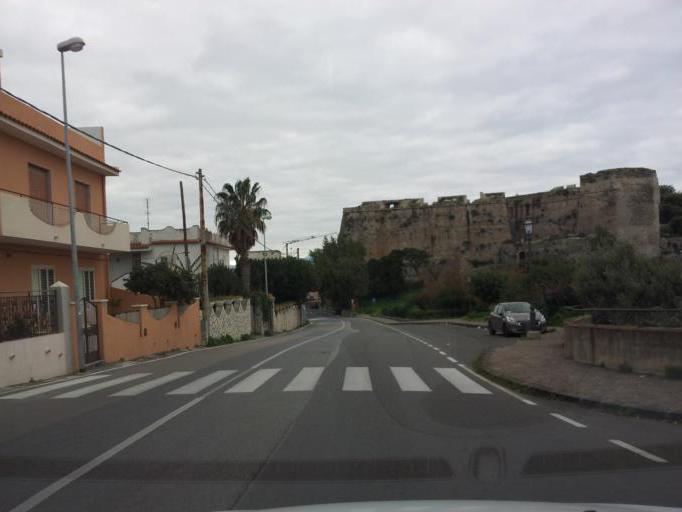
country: IT
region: Sicily
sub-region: Messina
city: Milazzo
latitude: 38.2334
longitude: 15.2448
